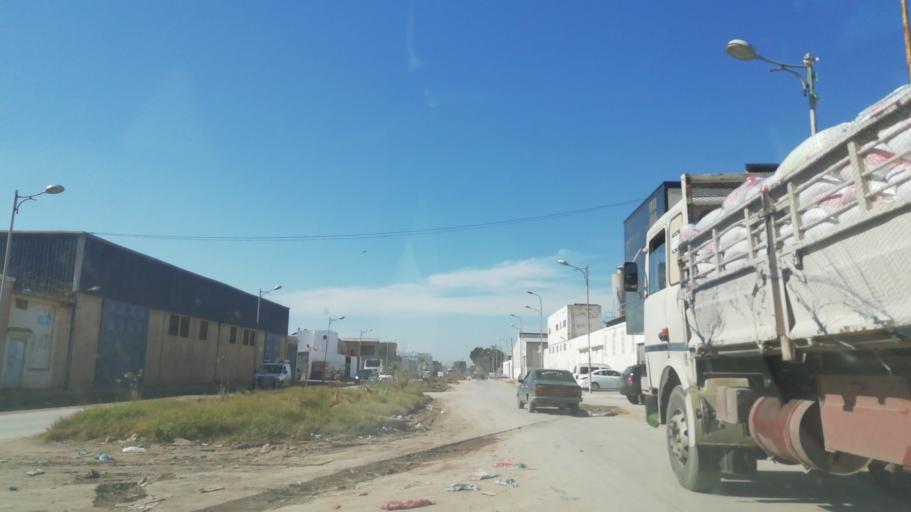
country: DZ
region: Oran
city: Es Senia
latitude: 35.6452
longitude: -0.5852
